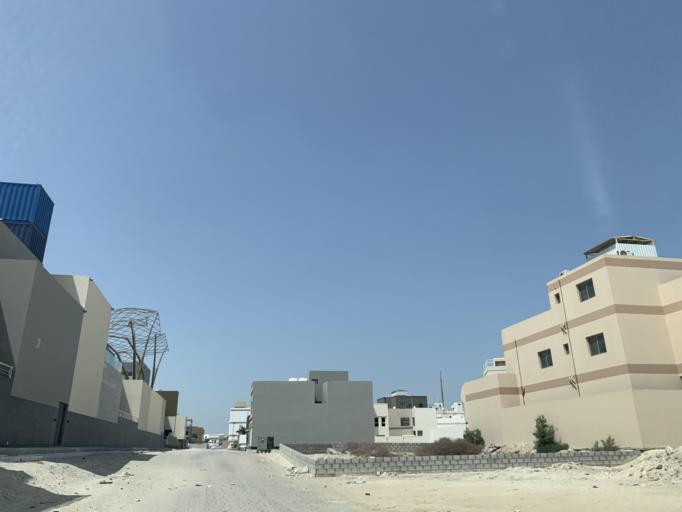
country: BH
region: Northern
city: Madinat `Isa
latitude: 26.1529
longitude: 50.5493
